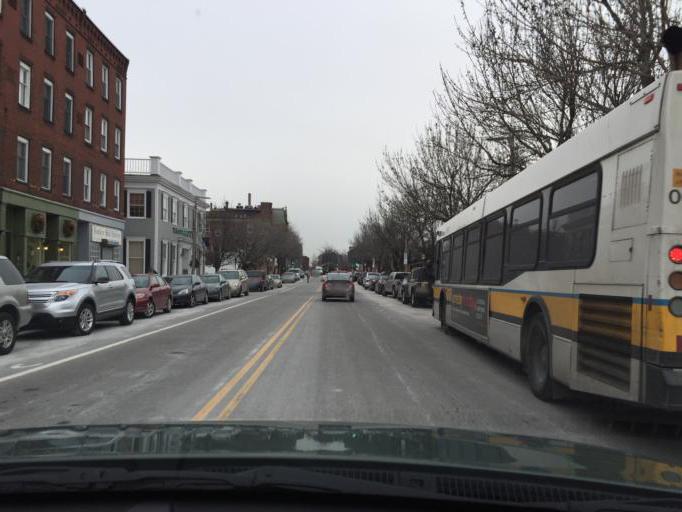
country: US
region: Massachusetts
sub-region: Suffolk County
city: Boston
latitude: 42.3764
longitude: -71.0657
